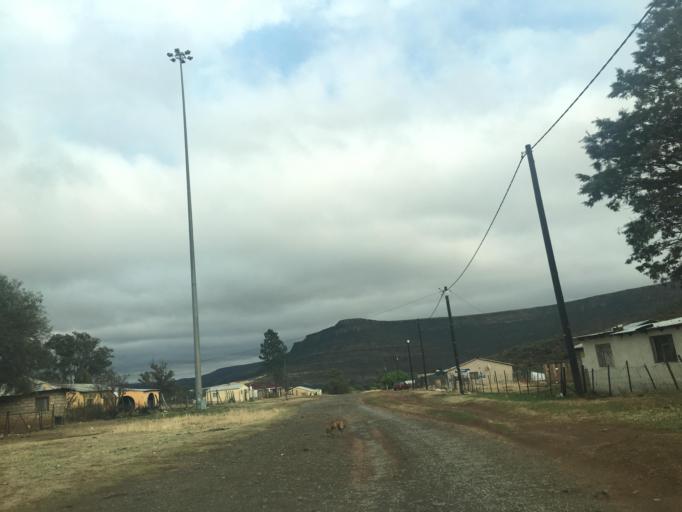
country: ZA
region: Eastern Cape
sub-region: Chris Hani District Municipality
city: Cala
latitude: -31.5188
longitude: 27.6942
